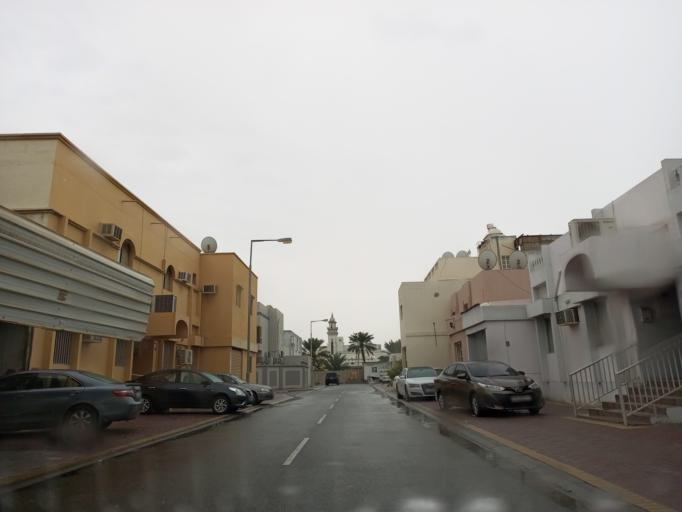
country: BH
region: Muharraq
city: Al Hadd
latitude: 26.2441
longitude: 50.6395
